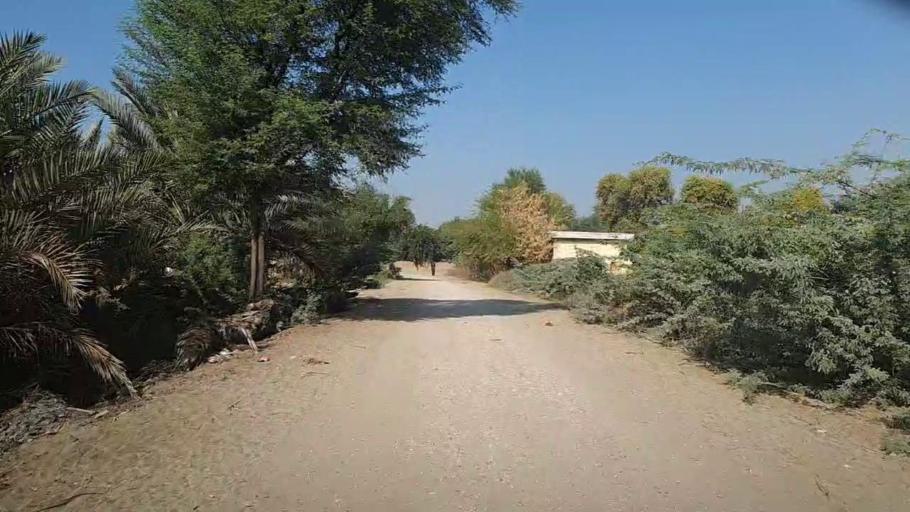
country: PK
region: Sindh
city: Bozdar
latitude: 27.1934
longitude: 68.6686
